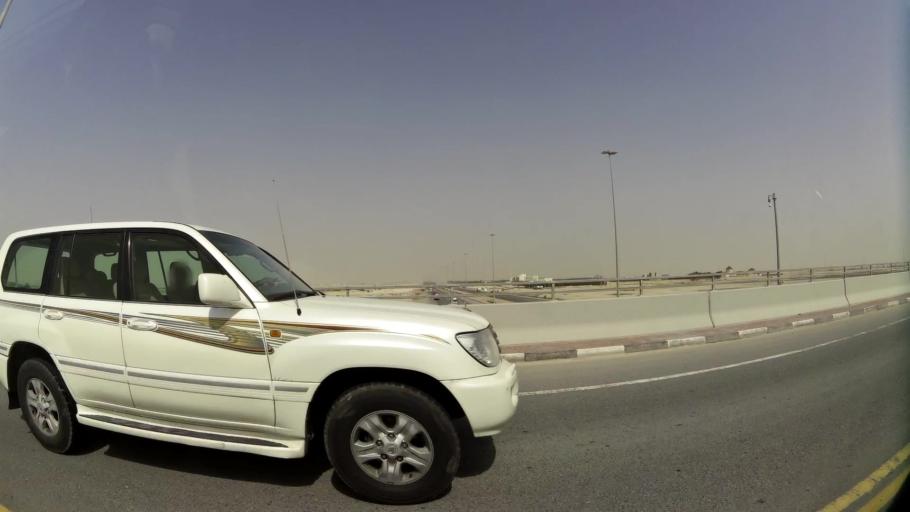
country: QA
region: Baladiyat ar Rayyan
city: Ar Rayyan
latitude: 25.1546
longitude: 51.2773
